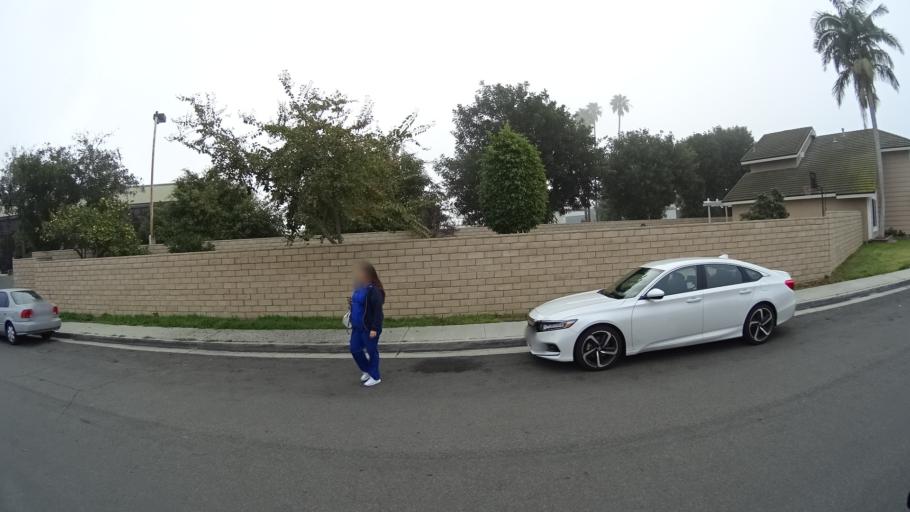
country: US
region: California
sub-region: Orange County
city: Stanton
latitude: 33.8165
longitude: -118.0079
